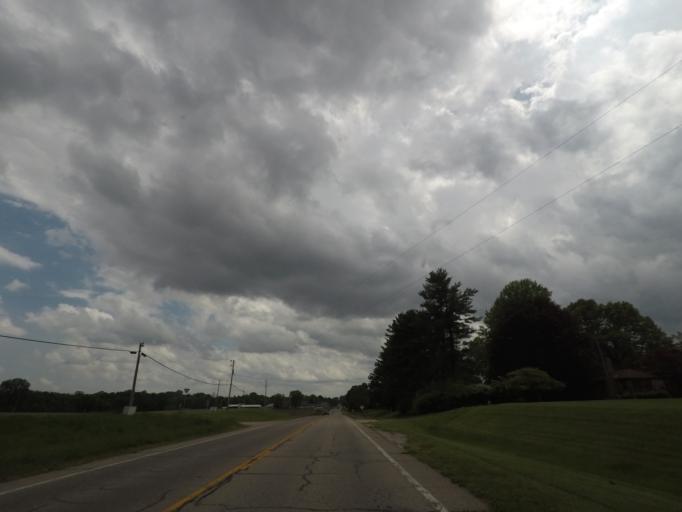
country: US
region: Illinois
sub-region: De Witt County
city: Clinton
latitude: 40.1668
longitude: -88.9605
